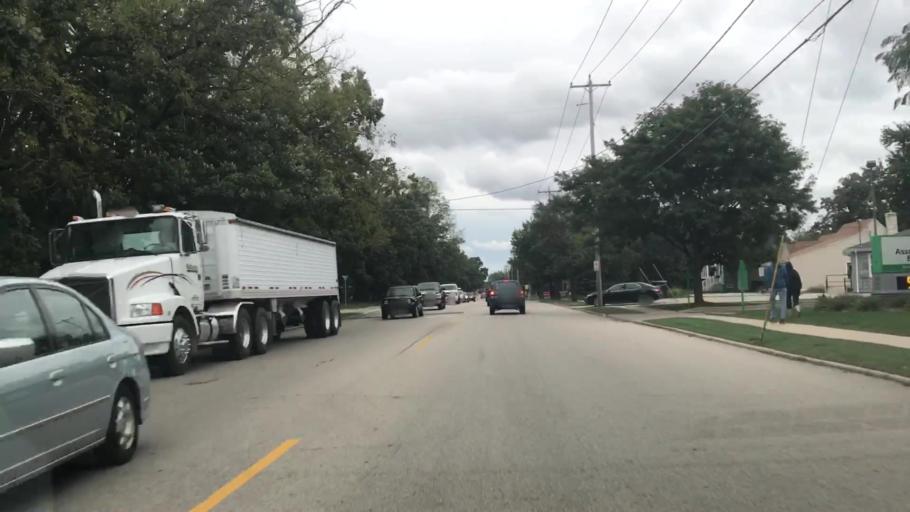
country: US
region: Wisconsin
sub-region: Waukesha County
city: Mukwonago
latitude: 42.8699
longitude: -88.3358
